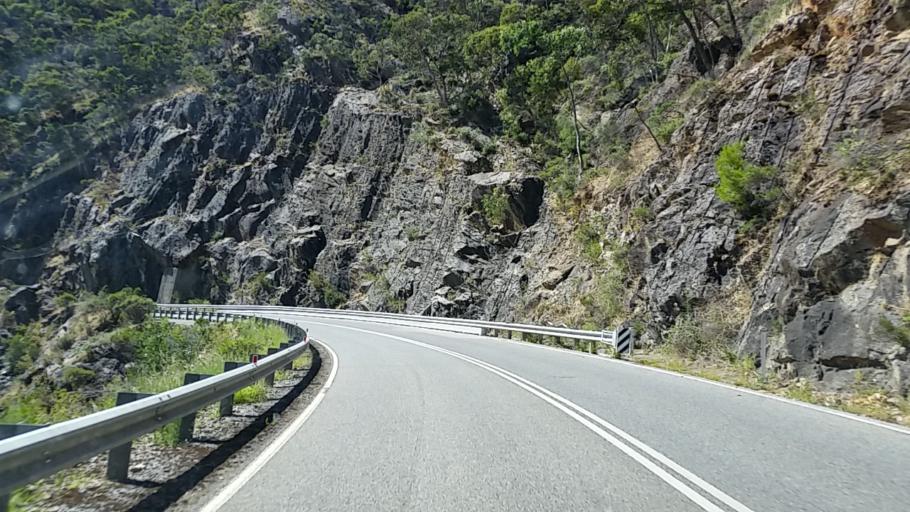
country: AU
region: South Australia
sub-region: Campbelltown
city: Athelstone
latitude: -34.8628
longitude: 138.7659
